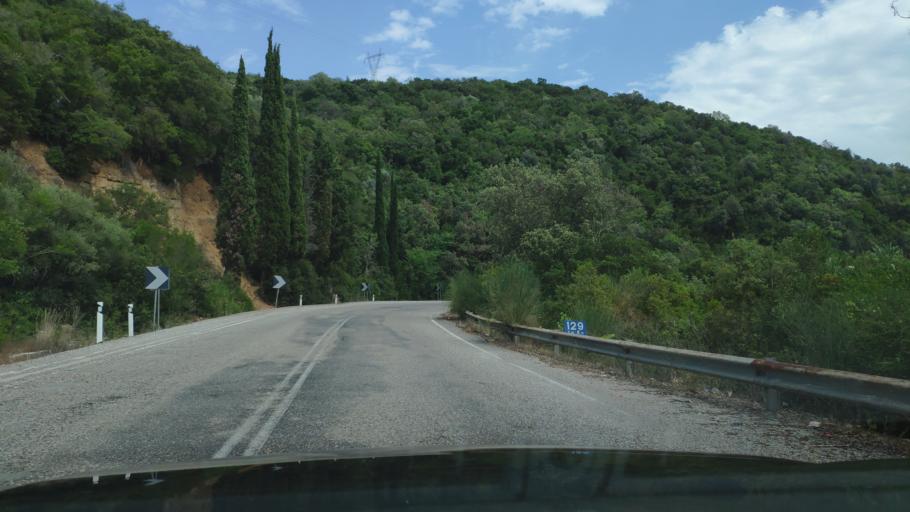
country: GR
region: West Greece
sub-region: Nomos Aitolias kai Akarnanias
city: Menidi
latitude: 39.0201
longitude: 21.1353
